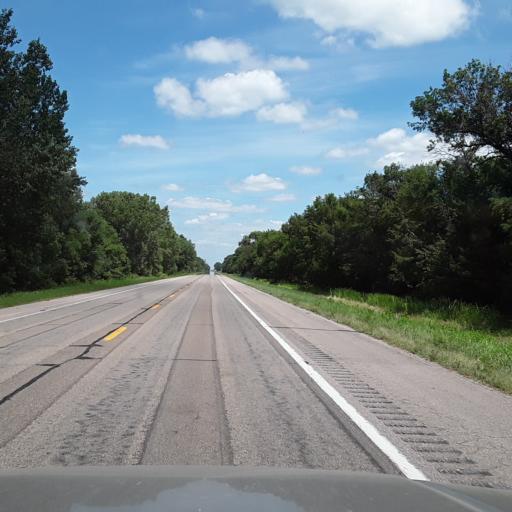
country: US
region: Nebraska
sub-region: Platte County
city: Columbus
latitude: 41.3764
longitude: -97.5213
